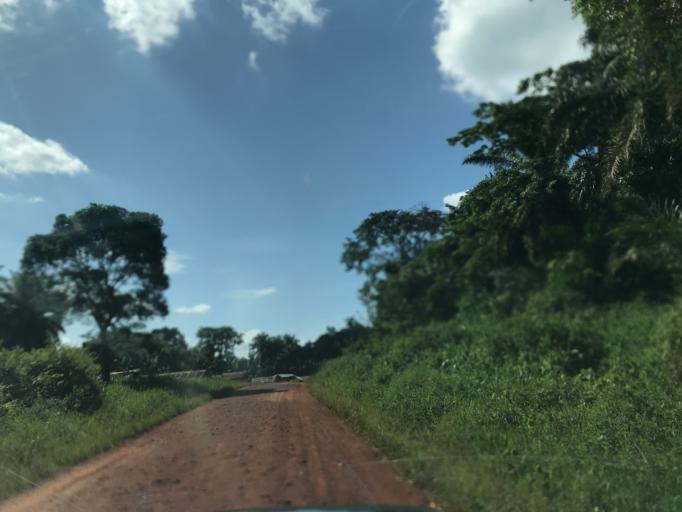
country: CD
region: Eastern Province
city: Kisangani
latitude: 1.2244
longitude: 25.2685
